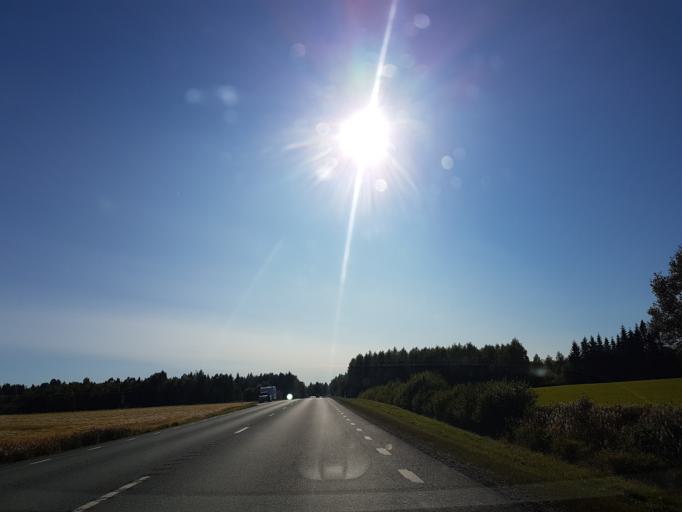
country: SE
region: Vaesterbotten
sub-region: Skelleftea Kommun
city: Burea
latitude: 64.3392
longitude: 21.2757
